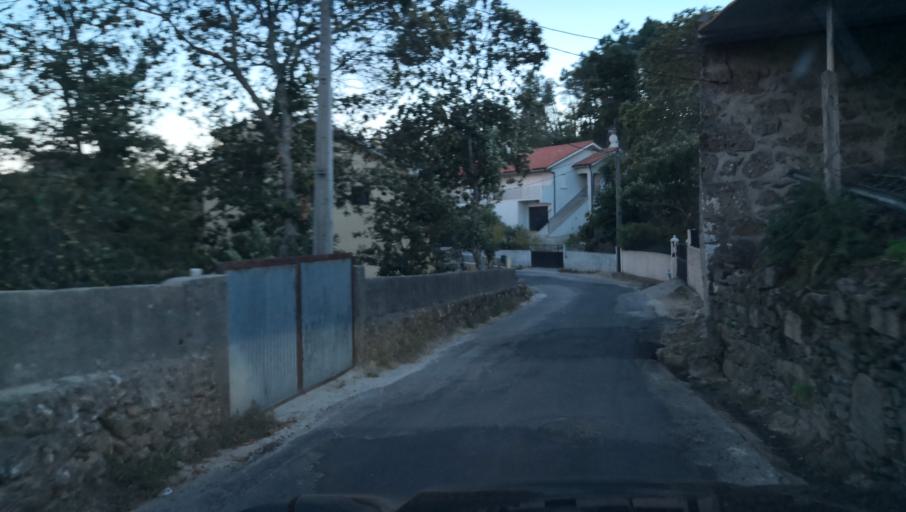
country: PT
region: Vila Real
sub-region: Santa Marta de Penaguiao
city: Santa Marta de Penaguiao
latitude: 41.2685
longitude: -7.8090
